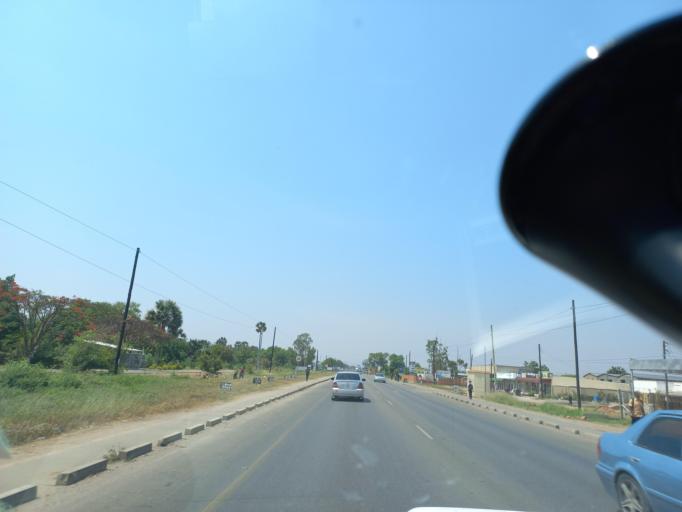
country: ZM
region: Lusaka
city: Kafue
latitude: -15.7660
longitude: 28.1792
